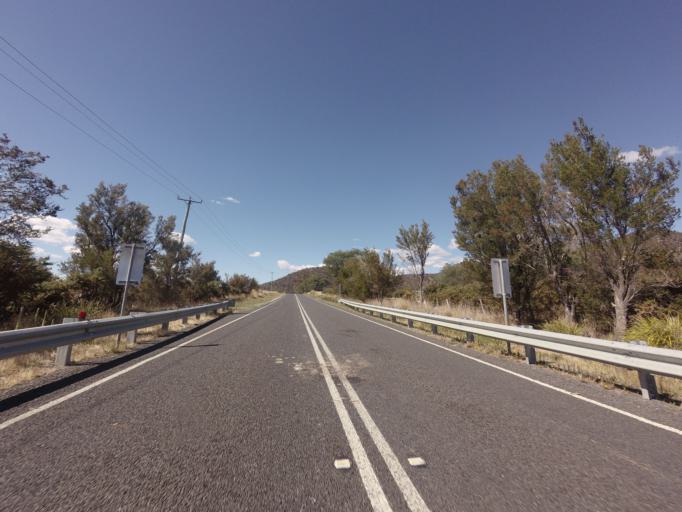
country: AU
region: Tasmania
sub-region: Break O'Day
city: St Helens
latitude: -41.6931
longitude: 147.8681
